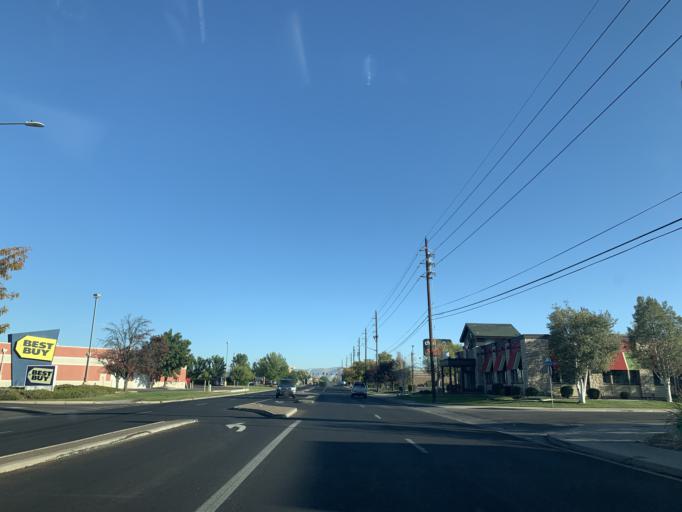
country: US
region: Colorado
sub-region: Mesa County
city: Redlands
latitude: 39.0889
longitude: -108.5988
